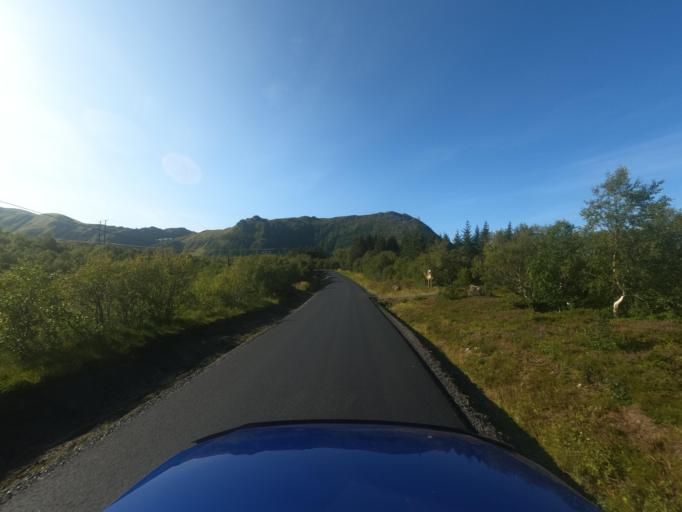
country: NO
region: Nordland
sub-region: Vestvagoy
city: Evjen
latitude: 68.2434
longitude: 13.8532
